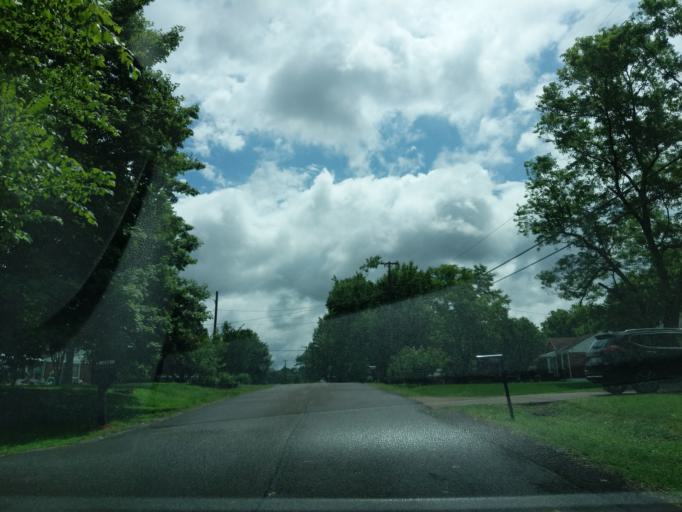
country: US
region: Tennessee
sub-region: Davidson County
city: Lakewood
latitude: 36.2363
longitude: -86.6772
